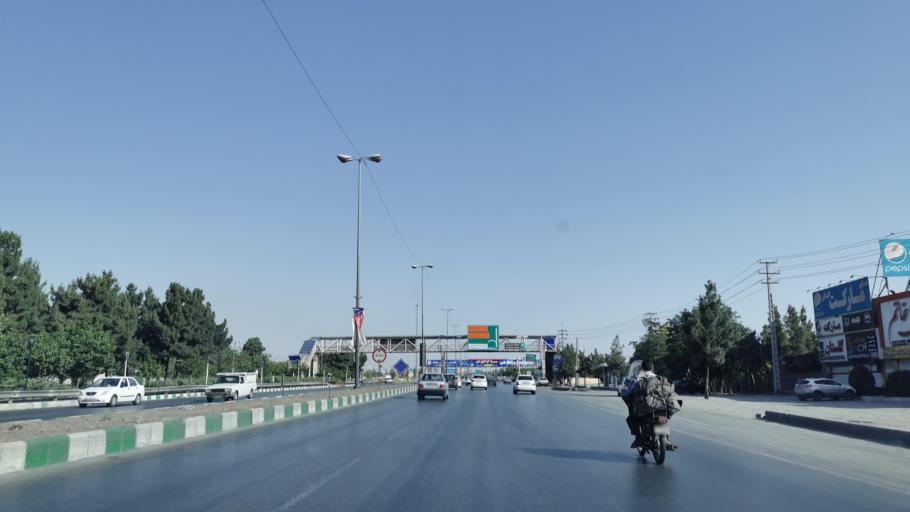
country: IR
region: Razavi Khorasan
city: Torqabeh
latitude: 36.4264
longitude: 59.4566
